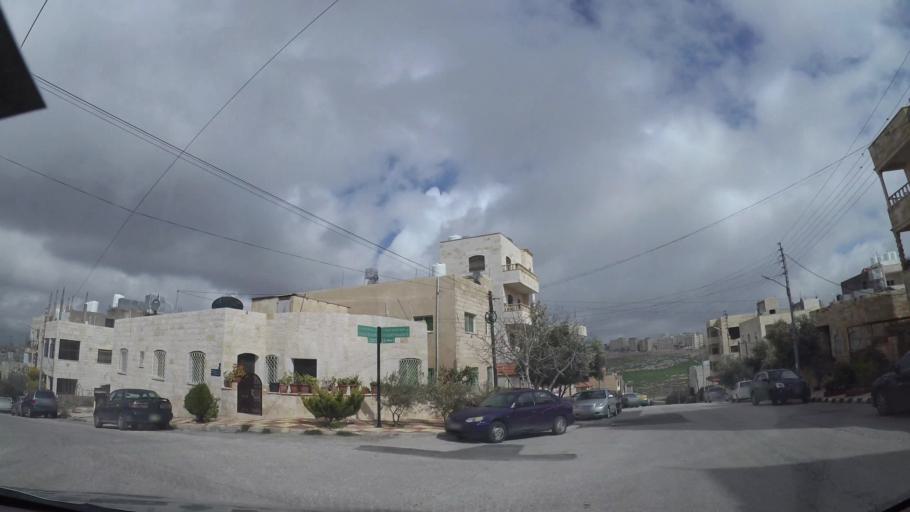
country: JO
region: Amman
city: Al Jubayhah
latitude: 32.0682
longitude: 35.8830
